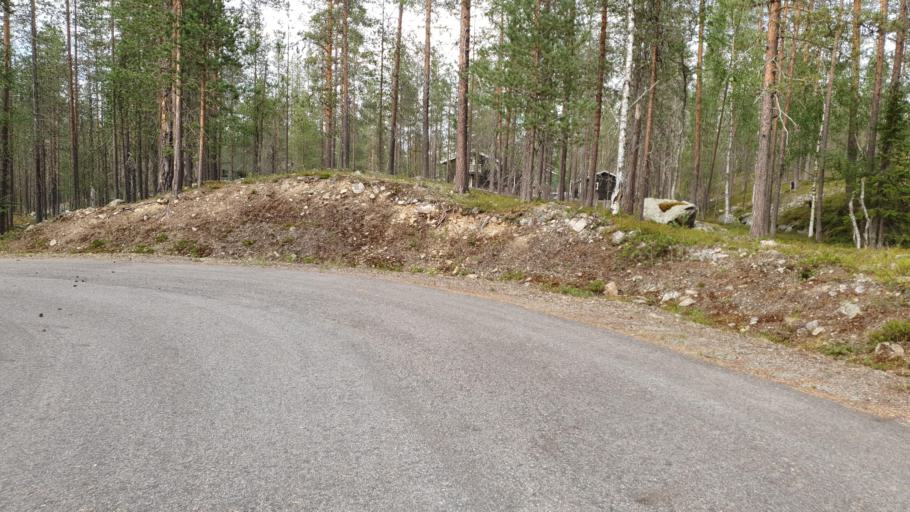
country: FI
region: Lapland
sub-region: Tunturi-Lappi
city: Kolari
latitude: 67.5914
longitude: 24.1310
